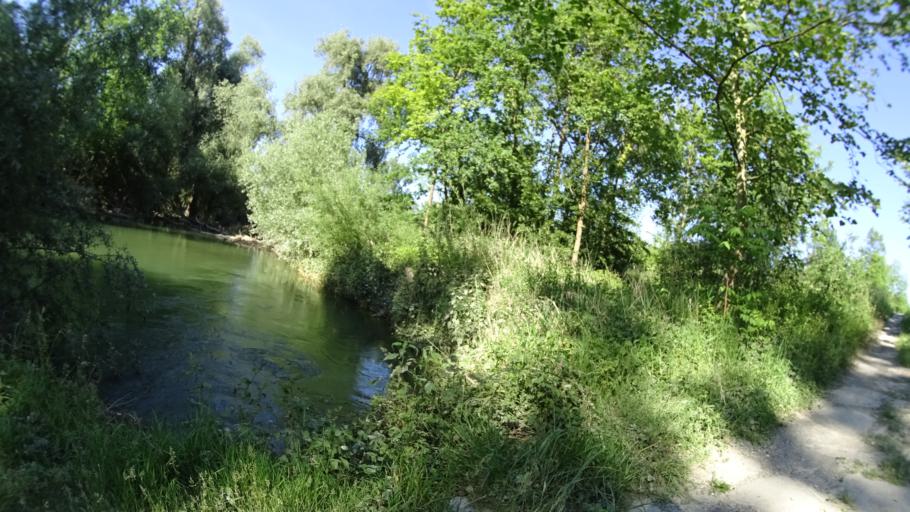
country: DE
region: Rheinland-Pfalz
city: Leimersheim
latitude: 49.1009
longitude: 8.3631
